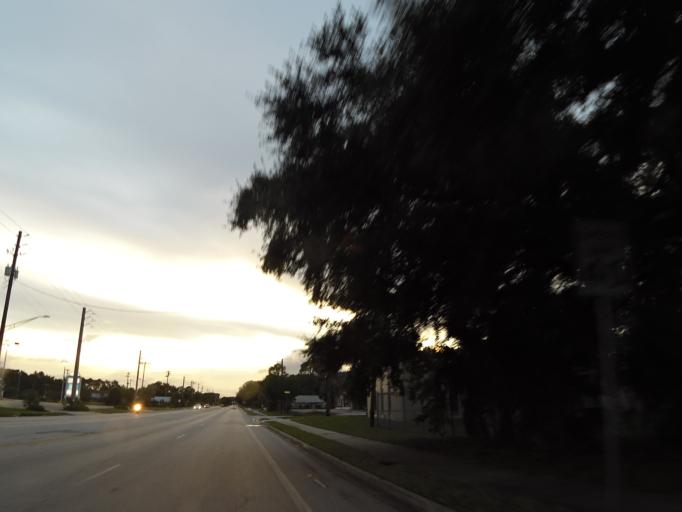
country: US
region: Florida
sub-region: Duval County
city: Jacksonville
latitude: 30.3665
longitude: -81.5880
